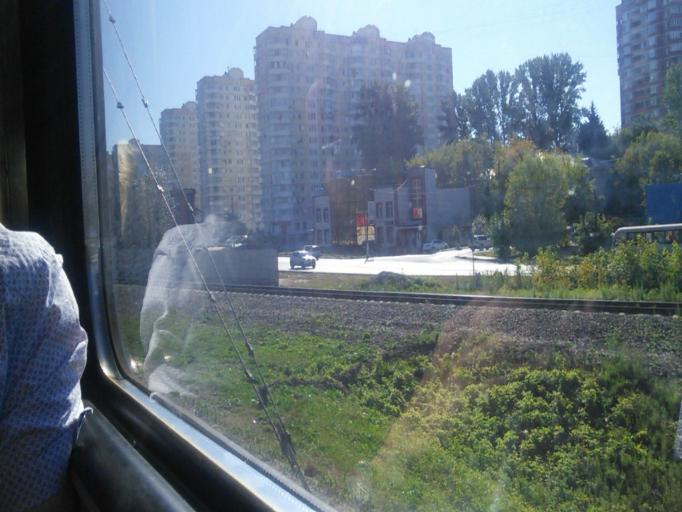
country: RU
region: Moskovskaya
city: Zheleznodorozhnyy
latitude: 55.7519
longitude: 37.9849
